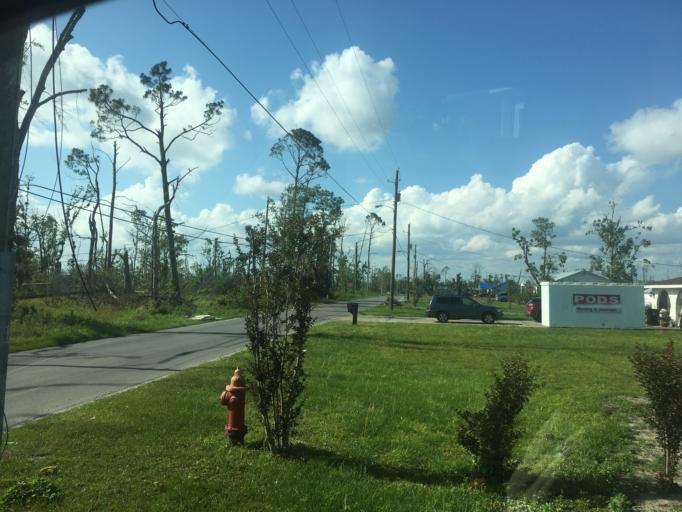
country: US
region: Florida
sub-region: Bay County
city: Cedar Grove
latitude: 30.1624
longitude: -85.6207
